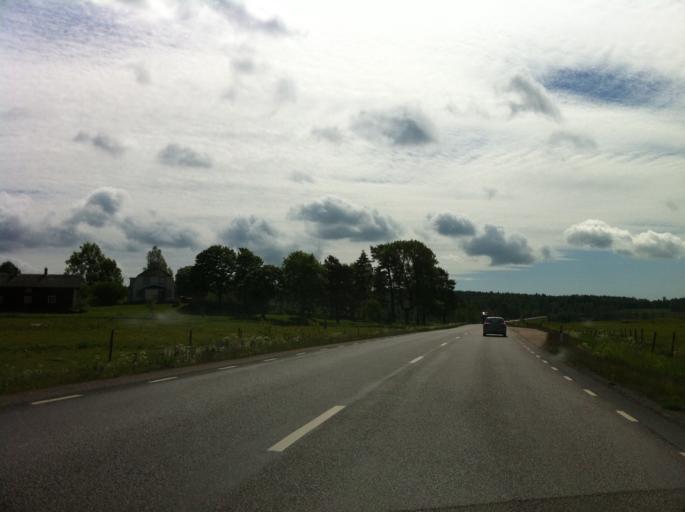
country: SE
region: Vaermland
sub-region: Saffle Kommun
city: Saeffle
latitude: 59.2120
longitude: 13.0210
